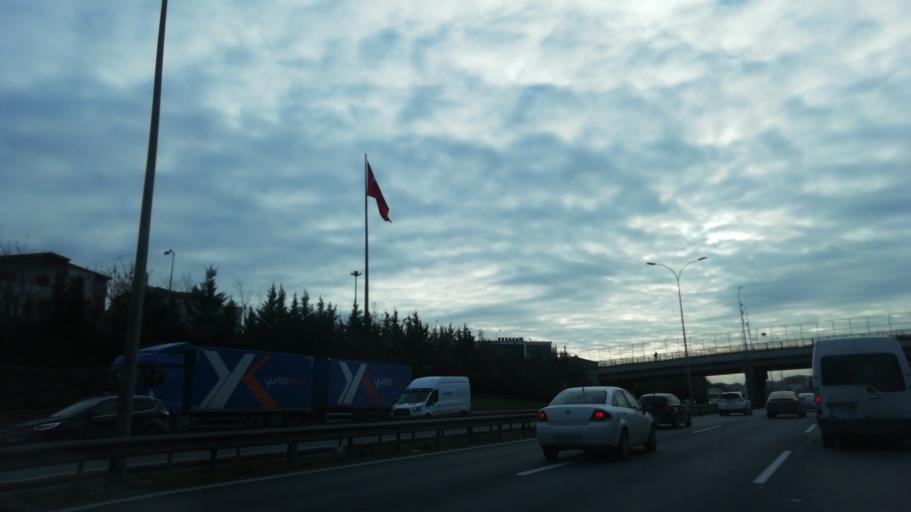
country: TR
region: Istanbul
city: Sultanbeyli
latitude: 40.9667
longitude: 29.2724
